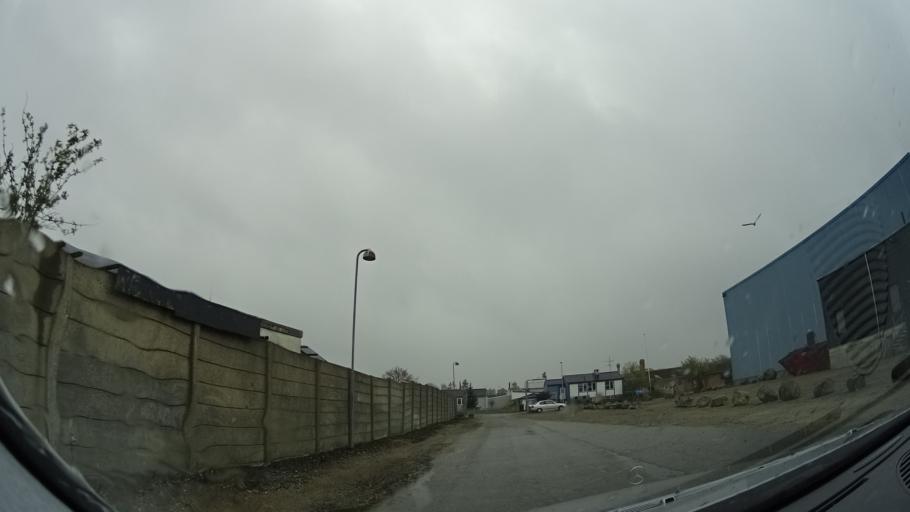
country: DK
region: Zealand
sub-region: Holbaek Kommune
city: Holbaek
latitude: 55.7198
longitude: 11.7229
